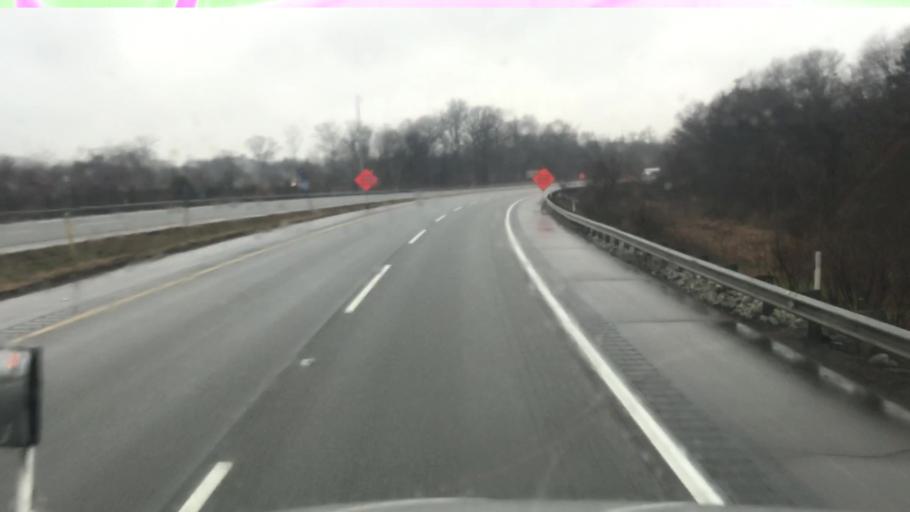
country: US
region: Indiana
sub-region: Saint Joseph County
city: Georgetown
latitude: 41.7169
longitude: -86.2375
